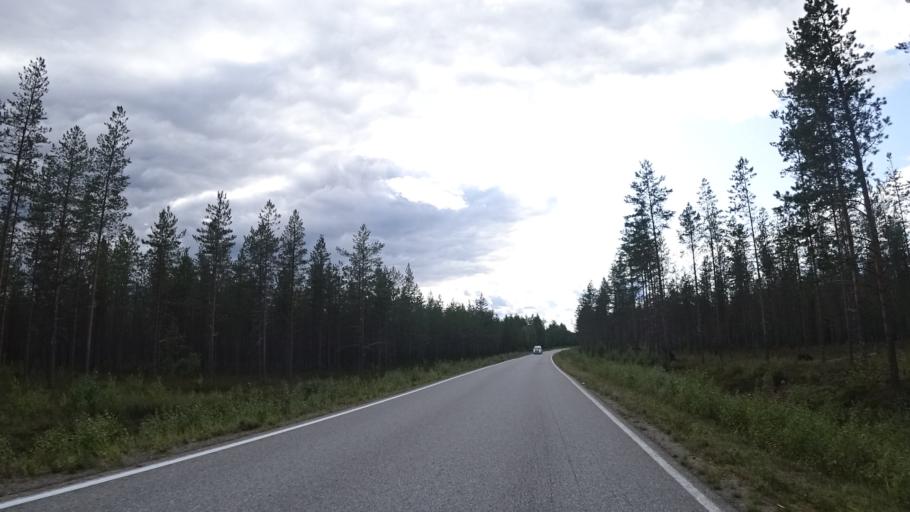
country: FI
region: North Karelia
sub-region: Joensuu
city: Ilomantsi
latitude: 62.4269
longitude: 31.0423
